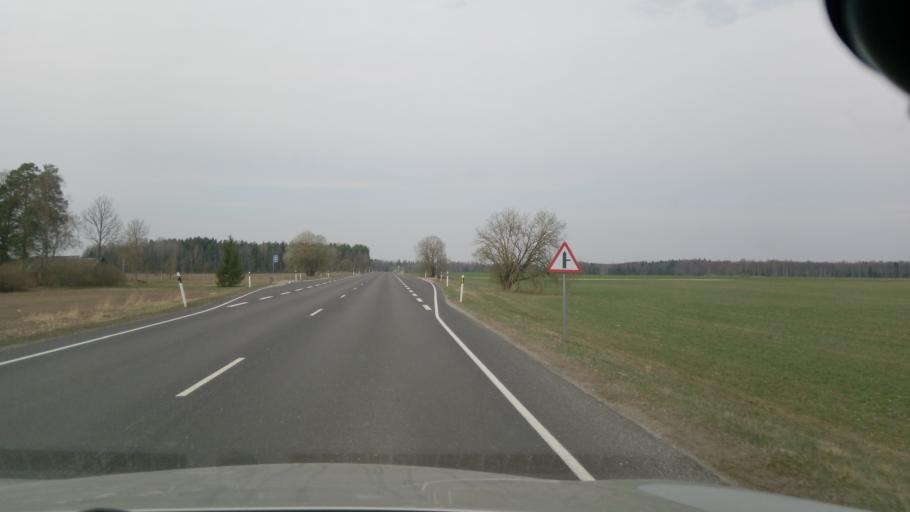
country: EE
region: Viljandimaa
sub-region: Vohma linn
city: Vohma
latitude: 58.7047
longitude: 25.6215
